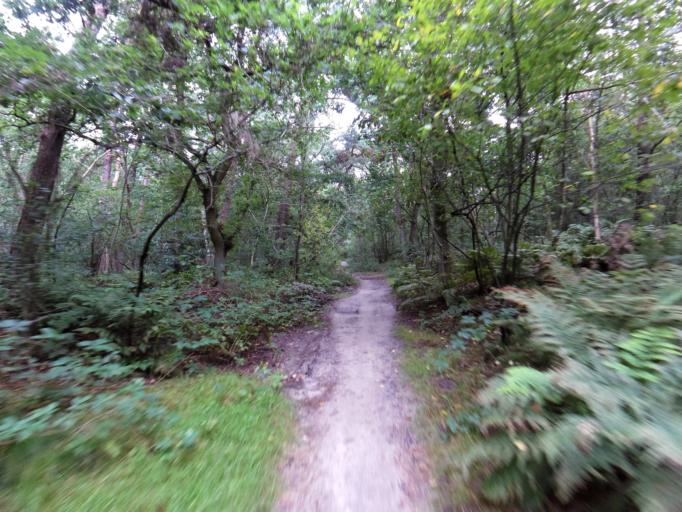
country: NL
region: North Brabant
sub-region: Gemeente Loon op Zand
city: Loon op Zand
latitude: 51.6376
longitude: 5.1130
